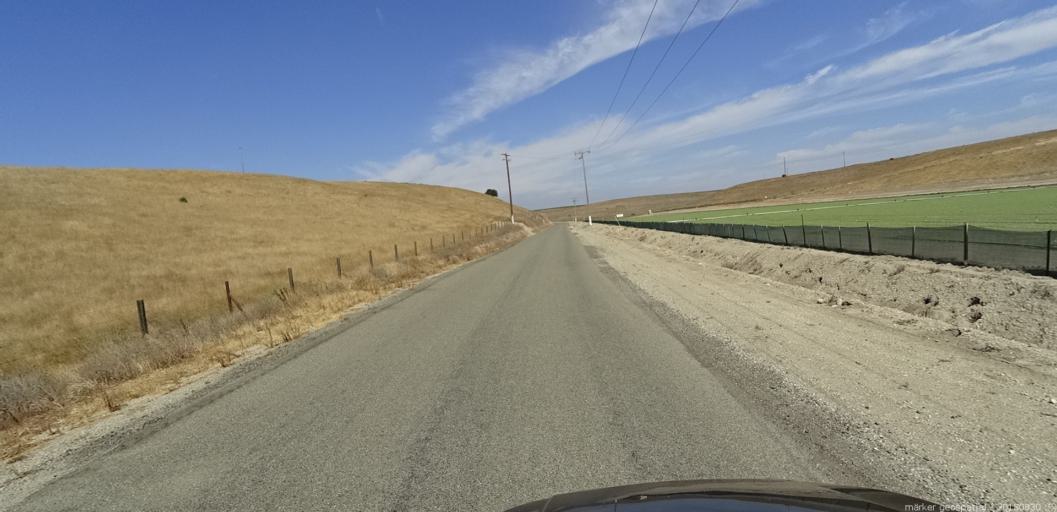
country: US
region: California
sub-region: Monterey County
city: King City
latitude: 36.1074
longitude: -121.0515
